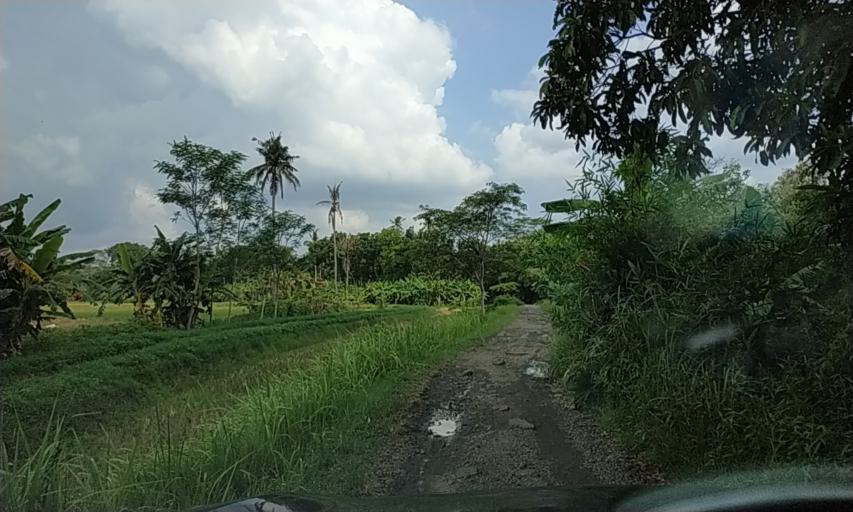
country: ID
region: Central Java
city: Bakung
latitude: -7.3400
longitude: 108.6677
